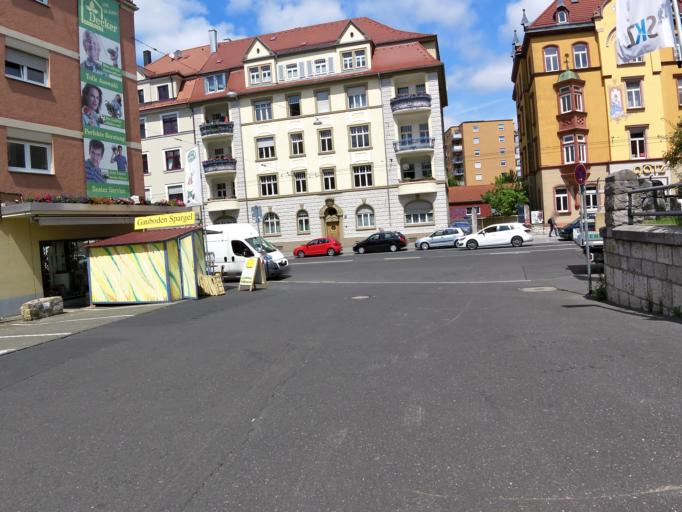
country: DE
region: Bavaria
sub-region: Regierungsbezirk Unterfranken
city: Hochberg
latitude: 49.7943
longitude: 9.9147
